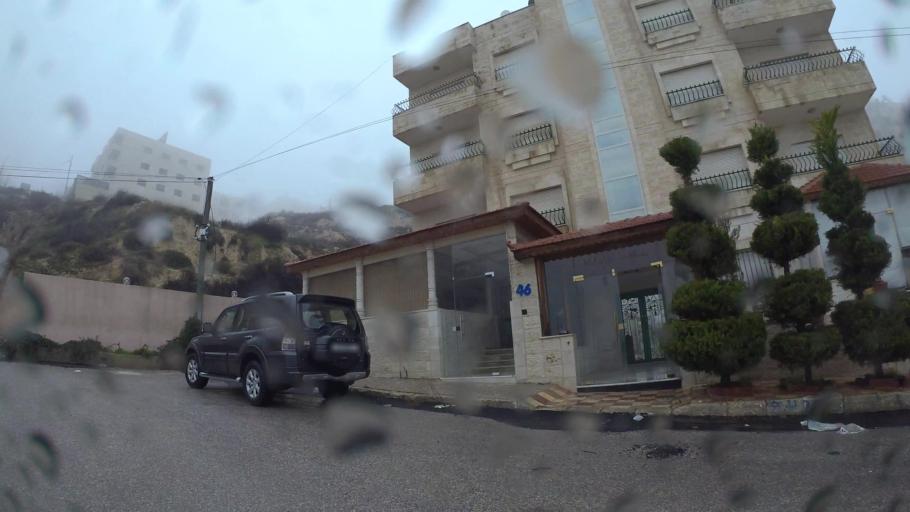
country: JO
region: Amman
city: Al Jubayhah
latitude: 32.0087
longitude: 35.8871
